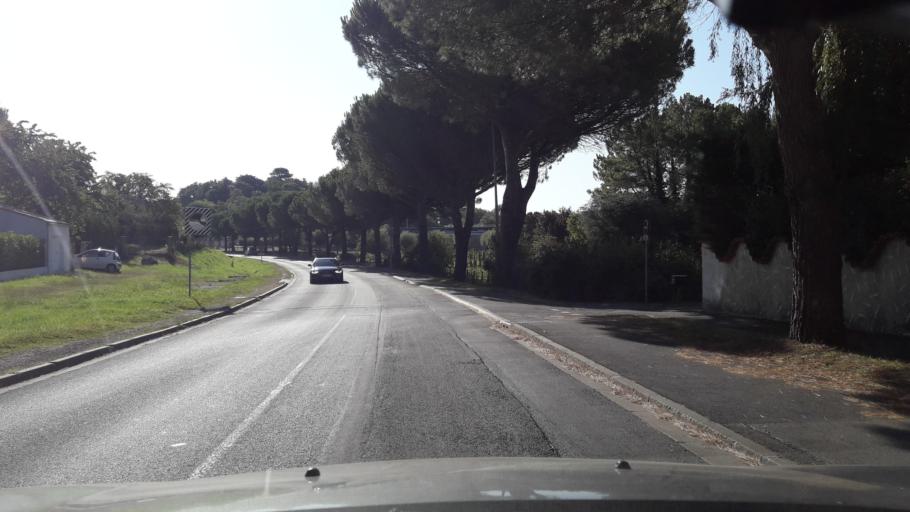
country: FR
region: Poitou-Charentes
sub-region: Departement de la Charente-Maritime
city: Les Mathes
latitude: 45.7160
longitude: -1.1503
